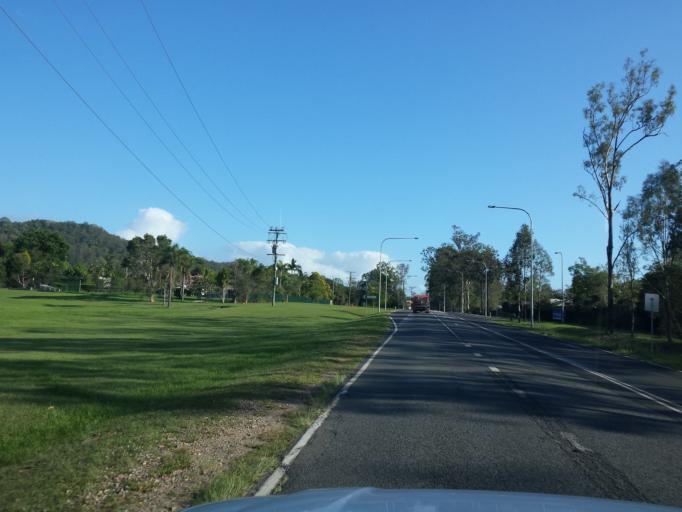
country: AU
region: Queensland
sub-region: Logan
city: Windaroo
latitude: -27.7592
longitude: 153.1857
